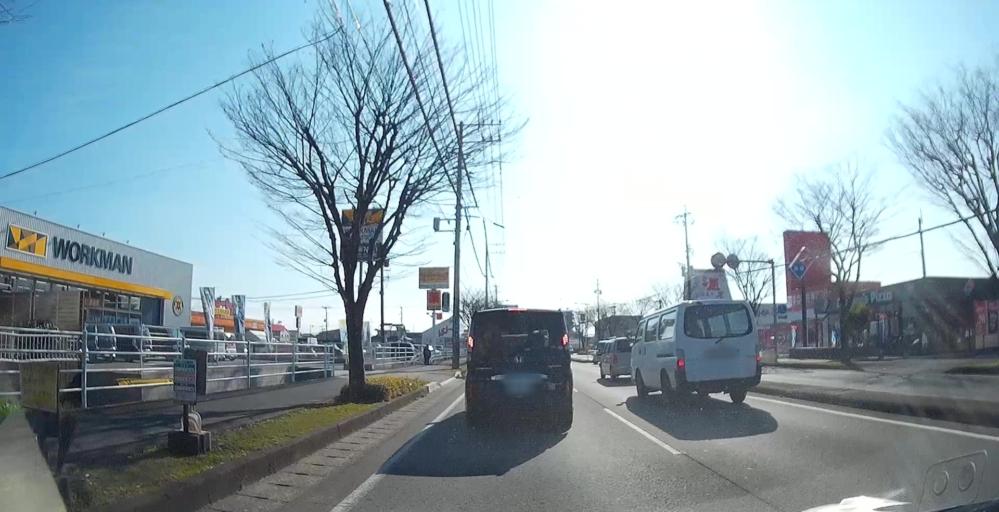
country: JP
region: Kumamoto
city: Kumamoto
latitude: 32.7773
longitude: 130.6731
